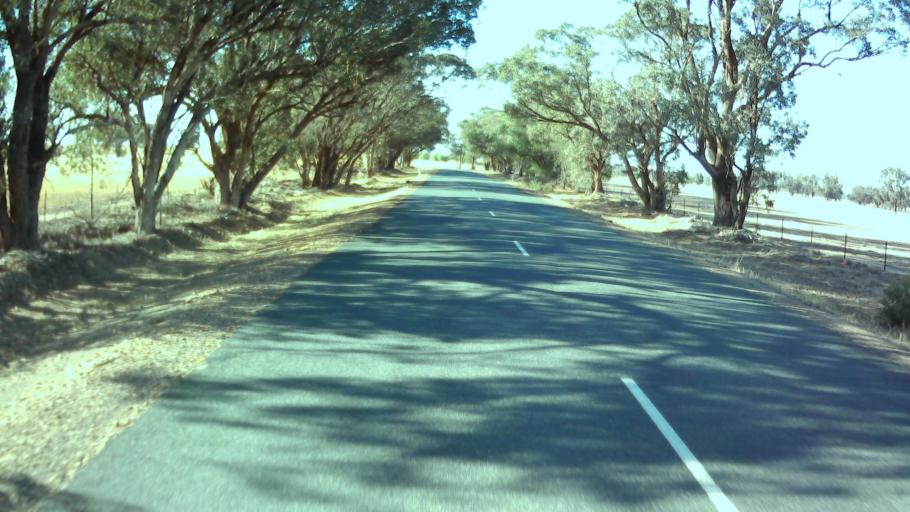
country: AU
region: New South Wales
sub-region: Weddin
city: Grenfell
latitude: -33.9742
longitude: 148.1410
